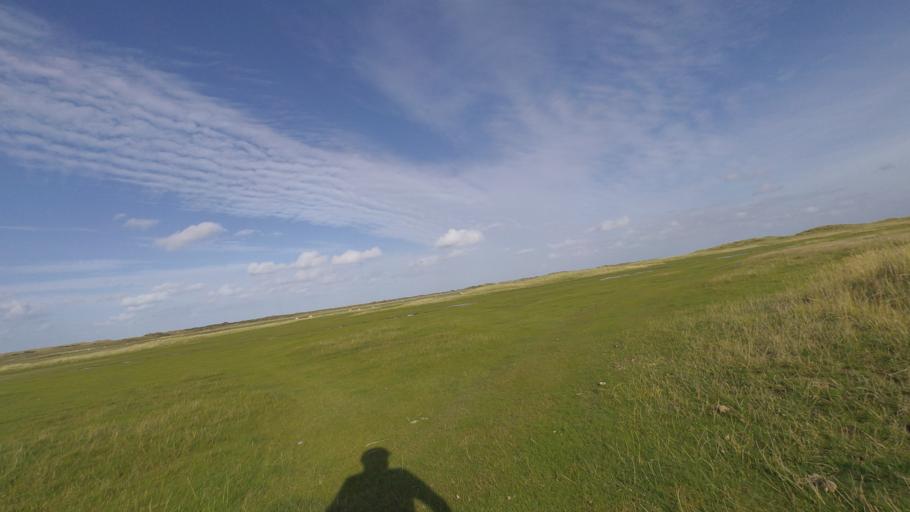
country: NL
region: Friesland
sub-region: Gemeente Ameland
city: Nes
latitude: 53.4558
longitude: 5.8659
